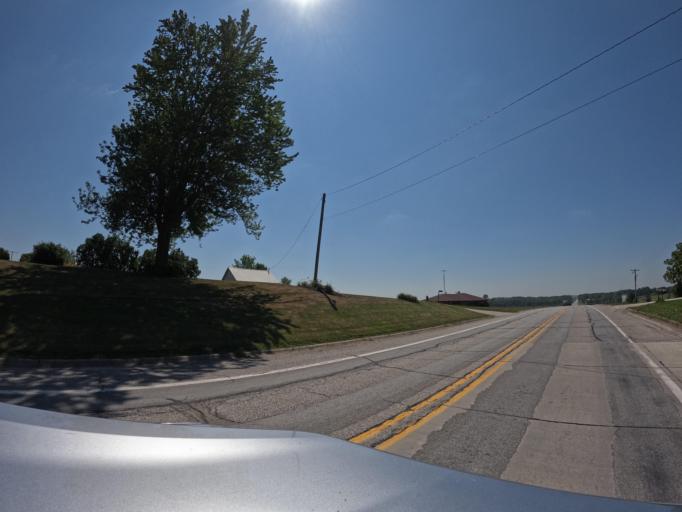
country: US
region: Iowa
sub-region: Keokuk County
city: Sigourney
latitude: 41.3190
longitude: -92.2052
